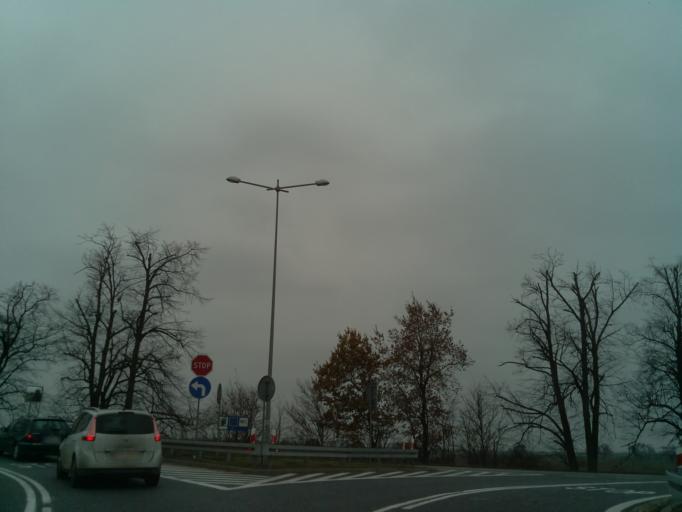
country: PL
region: Lower Silesian Voivodeship
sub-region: Powiat sredzki
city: Ciechow
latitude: 51.0435
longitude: 16.5965
